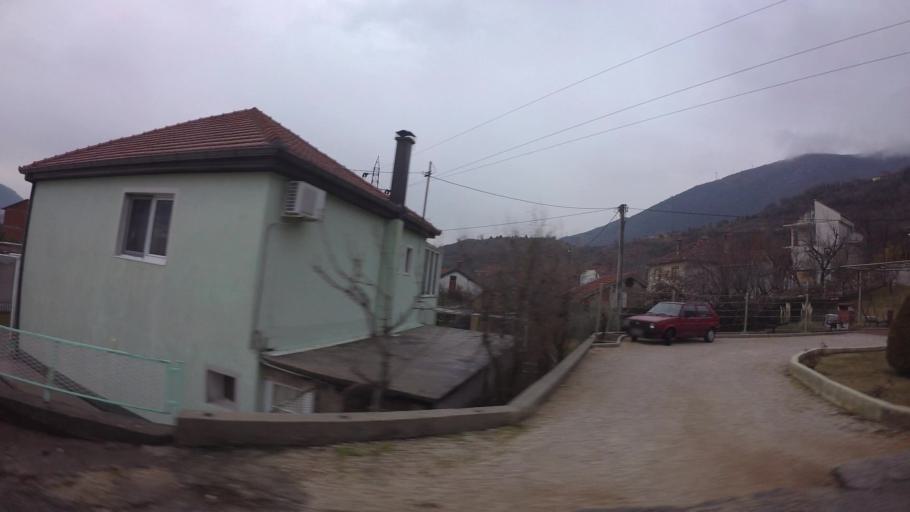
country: BA
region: Federation of Bosnia and Herzegovina
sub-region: Hercegovacko-Bosanski Kanton
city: Mostar
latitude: 43.3620
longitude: 17.8030
